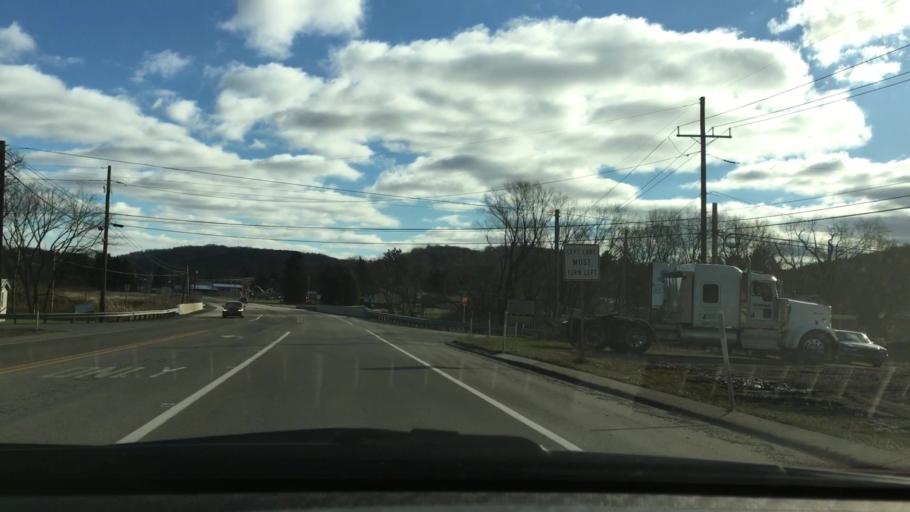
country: US
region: Pennsylvania
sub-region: Indiana County
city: Indiana
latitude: 40.6548
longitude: -79.2927
